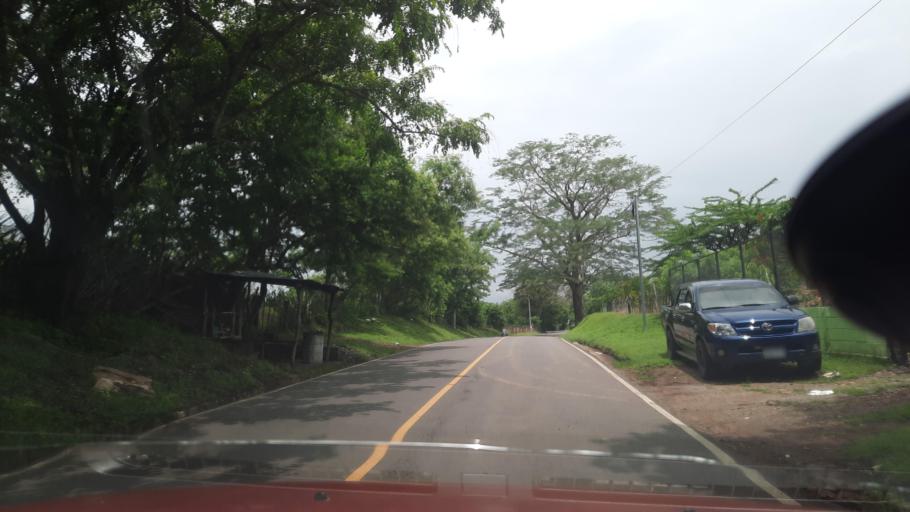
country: SV
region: La Union
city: Santa Rosa de Lima
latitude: 13.6455
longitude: -87.8582
